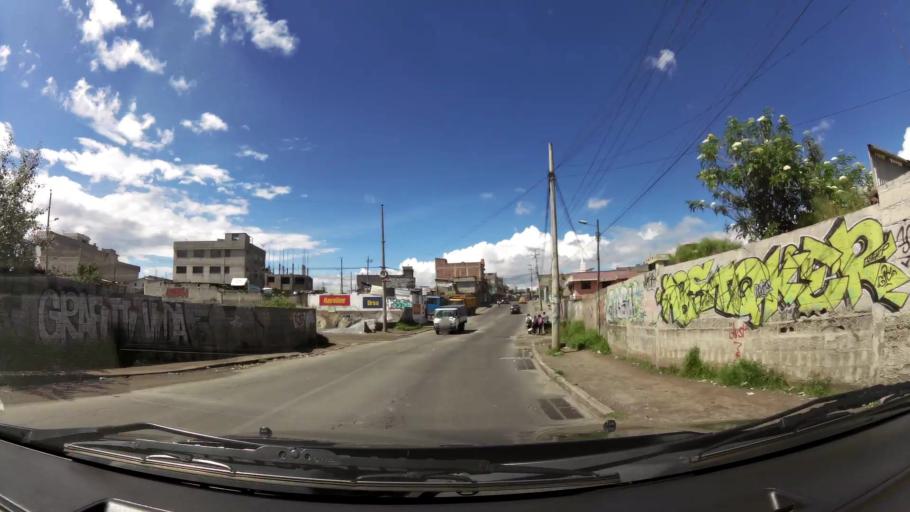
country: EC
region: Pichincha
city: Quito
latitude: -0.3096
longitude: -78.5591
